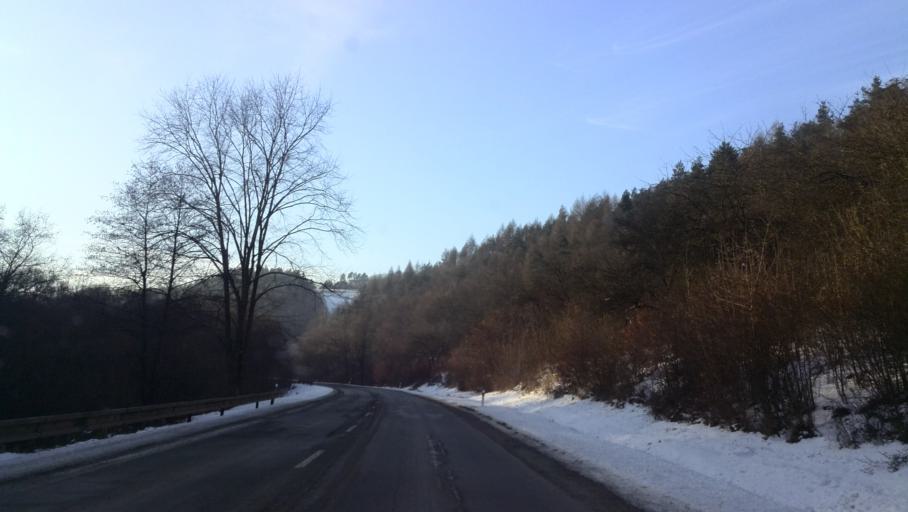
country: SK
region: Presovsky
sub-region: Okres Presov
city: Presov
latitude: 48.9639
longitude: 21.1289
